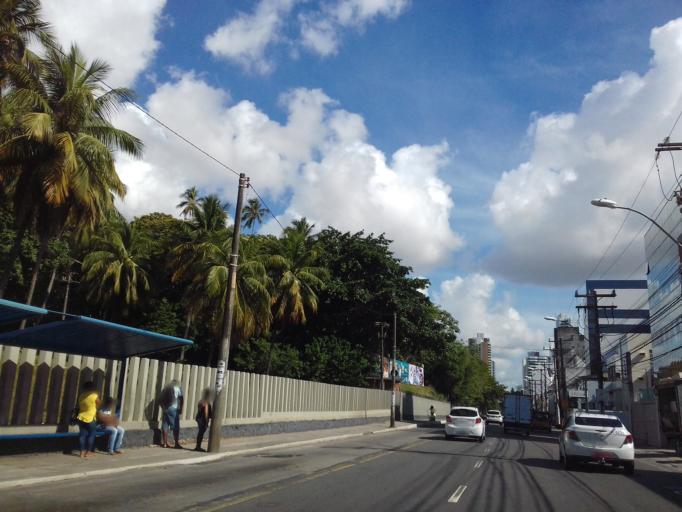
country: BR
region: Bahia
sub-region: Salvador
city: Salvador
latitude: -12.9961
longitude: -38.4547
